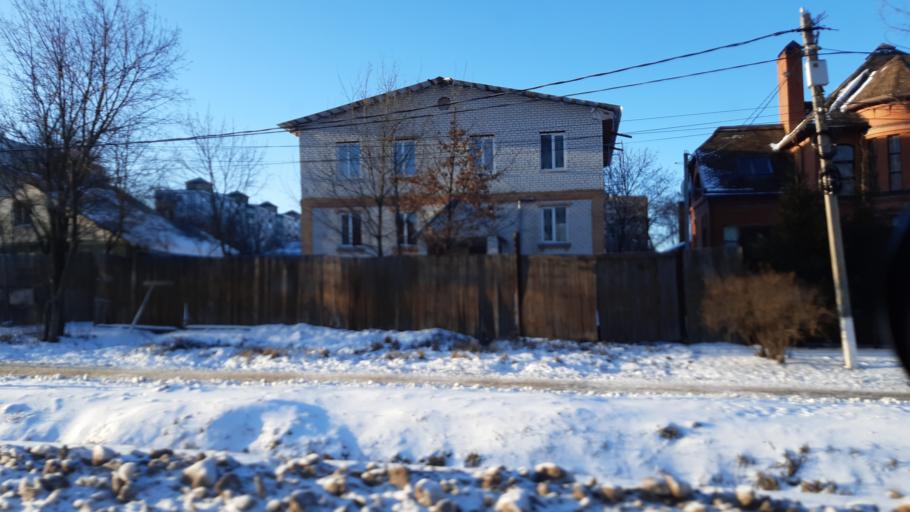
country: RU
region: Moskovskaya
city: Sergiyev Posad
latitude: 56.3295
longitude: 38.1527
